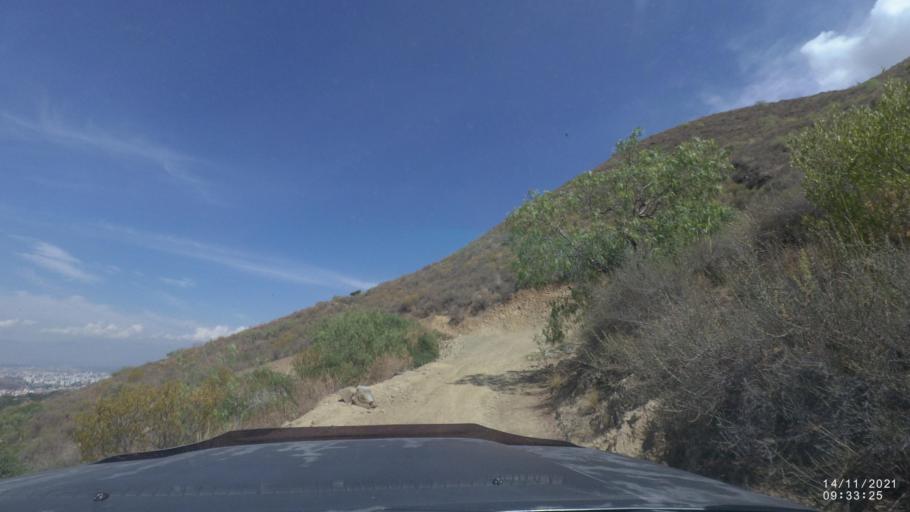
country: BO
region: Cochabamba
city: Cochabamba
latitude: -17.3667
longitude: -66.0889
